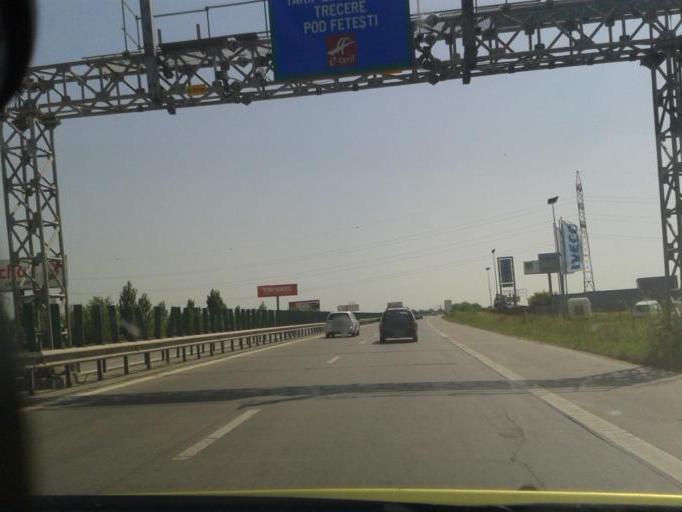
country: RO
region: Ilfov
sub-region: Comuna Glina
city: Catelu
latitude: 44.4086
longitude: 26.2406
